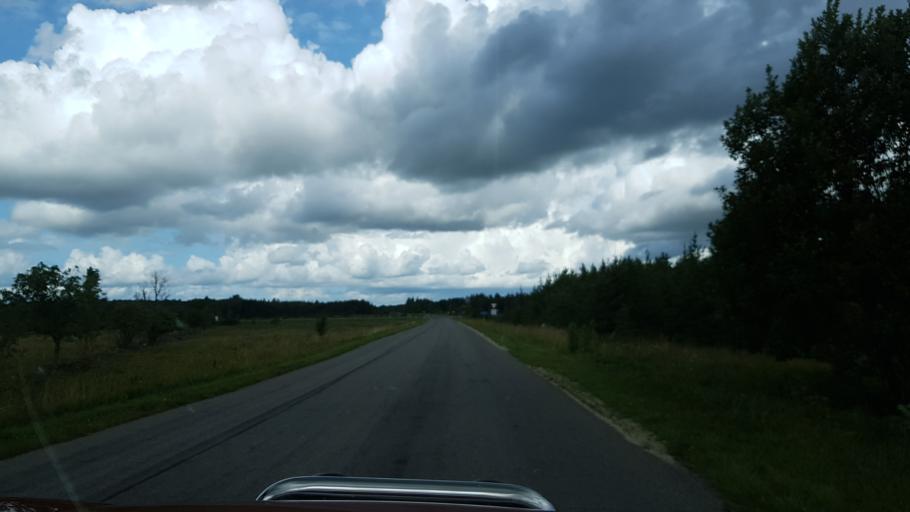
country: EE
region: Laeaene
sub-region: Lihula vald
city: Lihula
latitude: 58.6953
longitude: 23.8304
